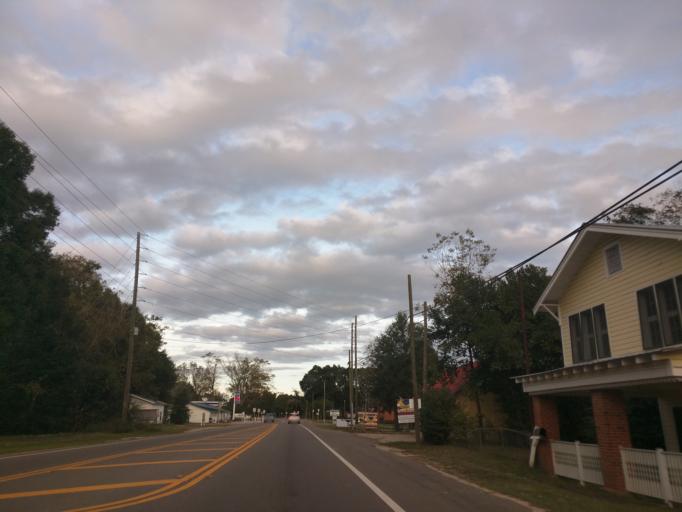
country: US
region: Florida
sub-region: Okaloosa County
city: Crestview
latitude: 30.7143
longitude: -86.7489
